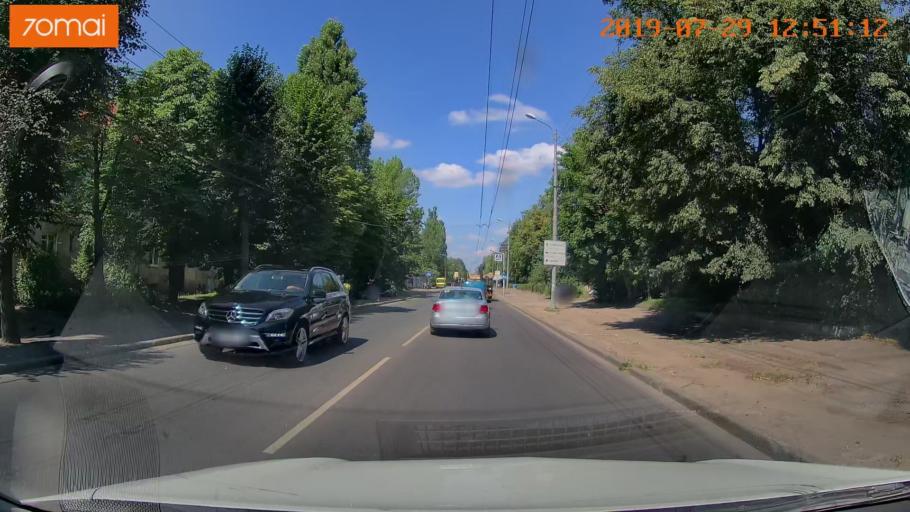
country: RU
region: Kaliningrad
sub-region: Gorod Kaliningrad
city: Kaliningrad
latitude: 54.6914
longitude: 20.5294
